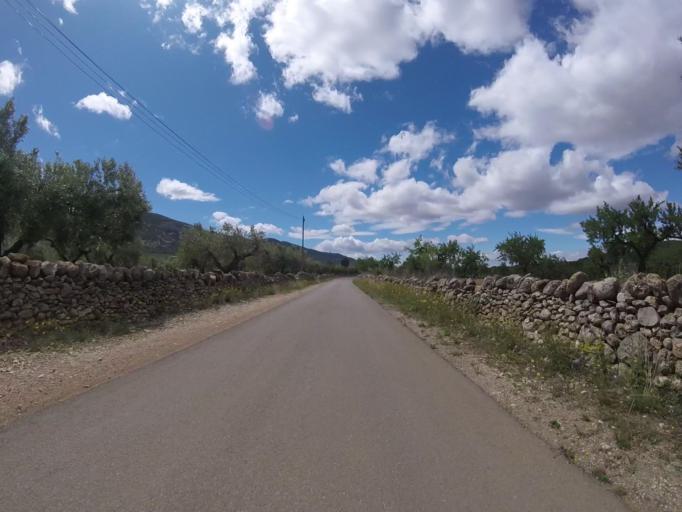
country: ES
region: Valencia
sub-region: Provincia de Castello
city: Sierra-Engarceran
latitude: 40.2913
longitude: -0.0557
